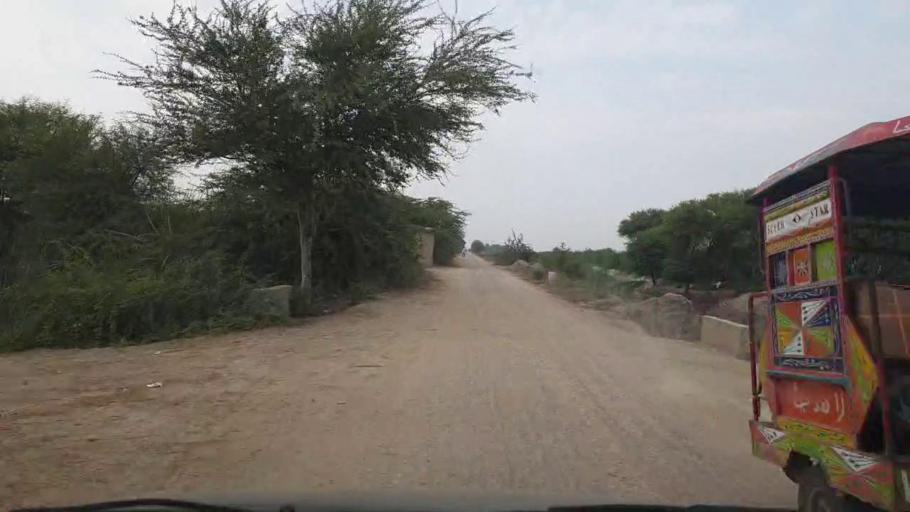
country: PK
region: Sindh
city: Kario
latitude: 24.6050
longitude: 68.5982
